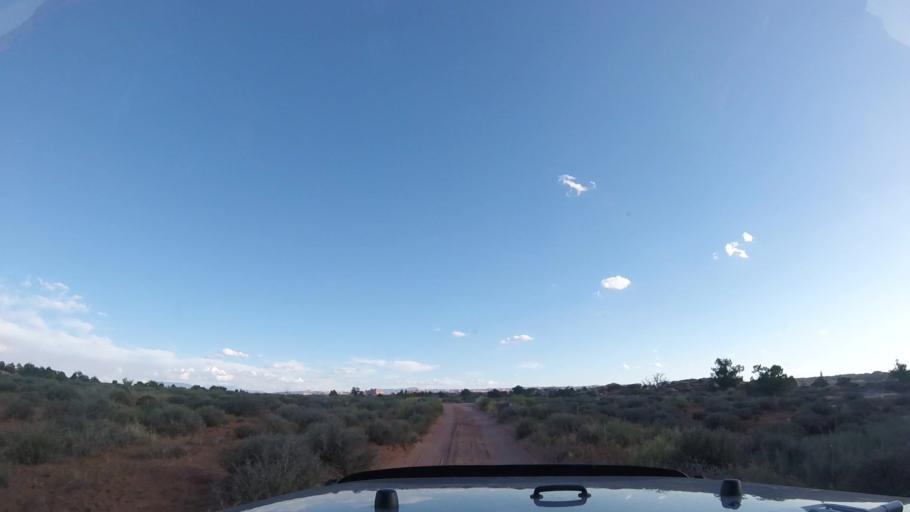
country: US
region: Utah
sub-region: Grand County
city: Moab
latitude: 38.2015
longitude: -109.7831
